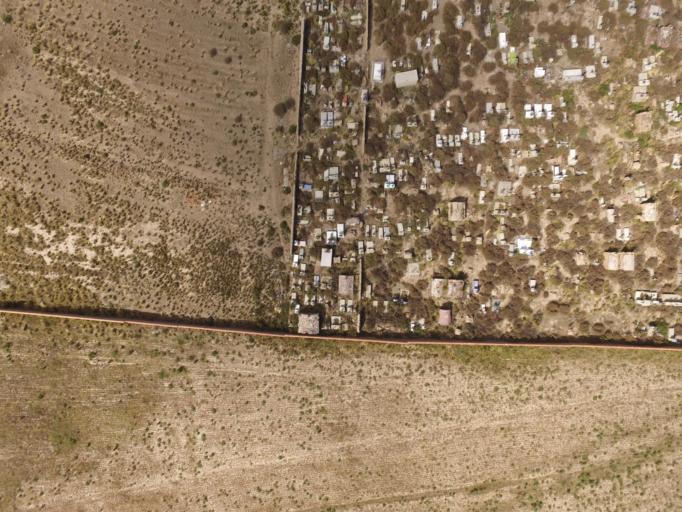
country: BO
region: Oruro
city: Challapata
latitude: -18.6920
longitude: -66.7607
